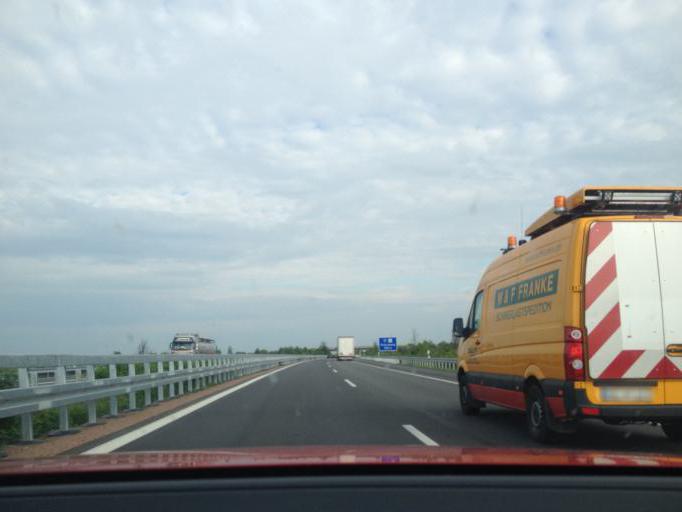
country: DE
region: Saxony-Anhalt
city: Gutenberg
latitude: 51.5644
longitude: 11.9940
